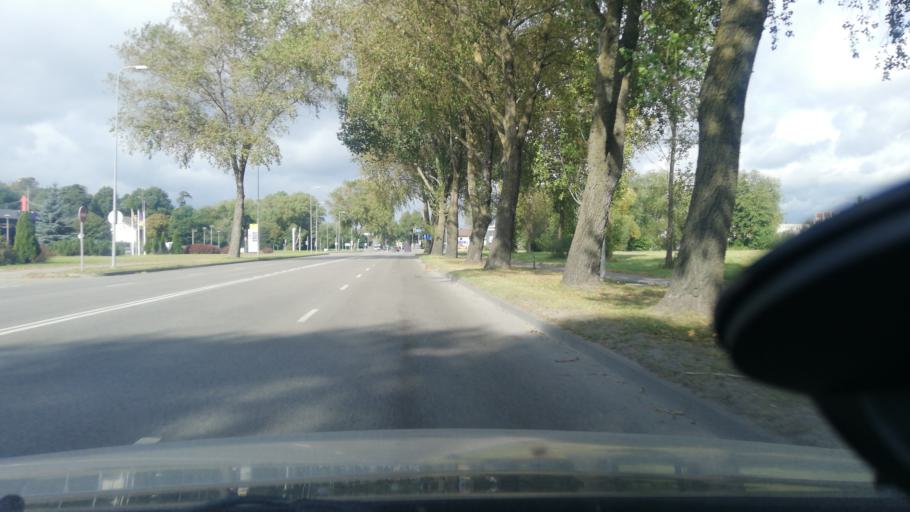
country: LT
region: Klaipedos apskritis
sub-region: Klaipeda
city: Klaipeda
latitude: 55.6690
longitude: 21.1602
